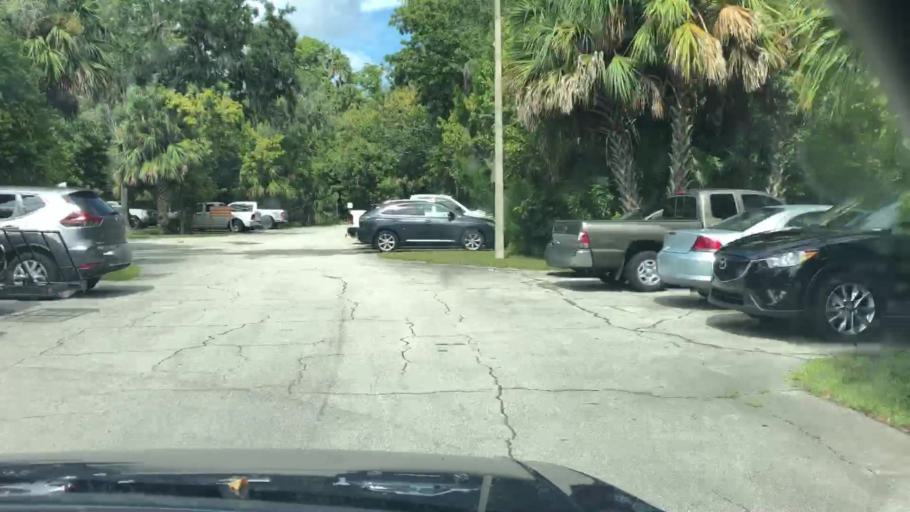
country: US
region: Florida
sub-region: Volusia County
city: Daytona Beach
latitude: 29.1928
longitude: -81.0367
